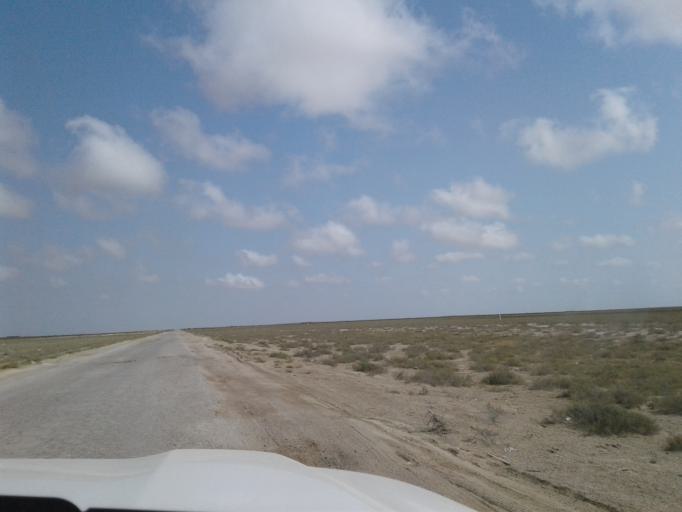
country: IR
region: Golestan
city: Gomishan
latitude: 37.6166
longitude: 53.9267
